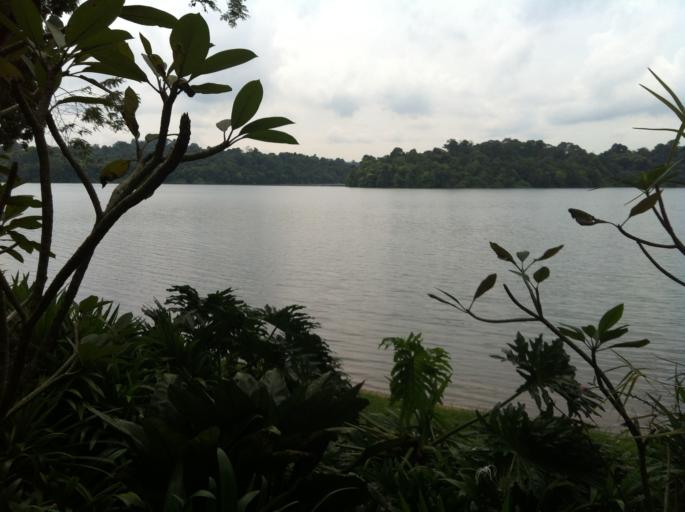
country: MY
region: Johor
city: Johor Bahru
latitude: 1.4018
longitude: 103.7953
